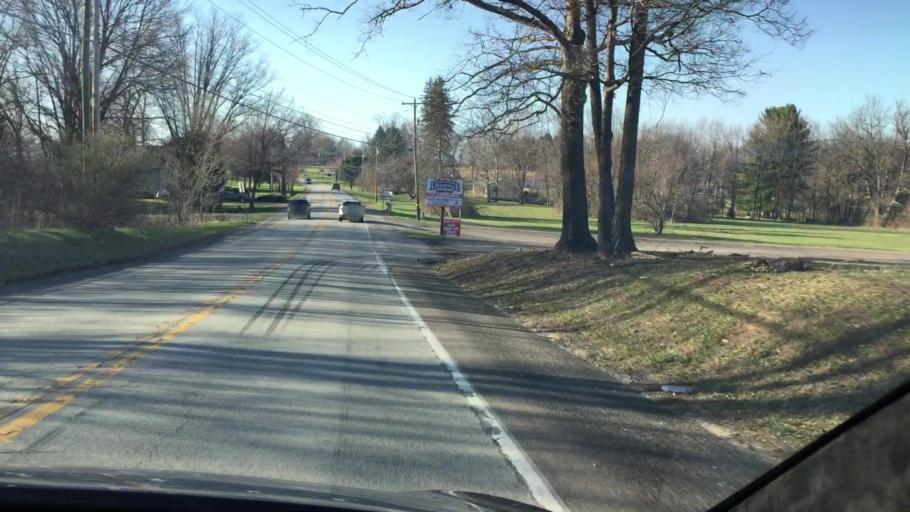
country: US
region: Pennsylvania
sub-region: Butler County
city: Saxonburg
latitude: 40.7397
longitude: -79.7635
